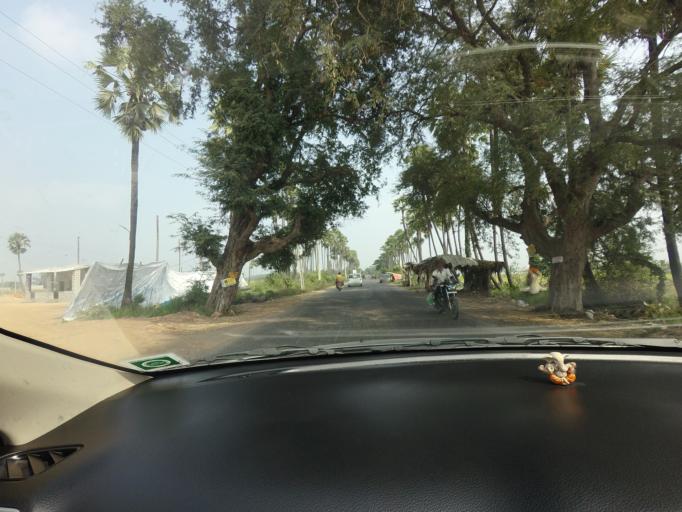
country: IN
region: Andhra Pradesh
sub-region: Krishna
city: Kankipadu
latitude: 16.4541
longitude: 80.7904
